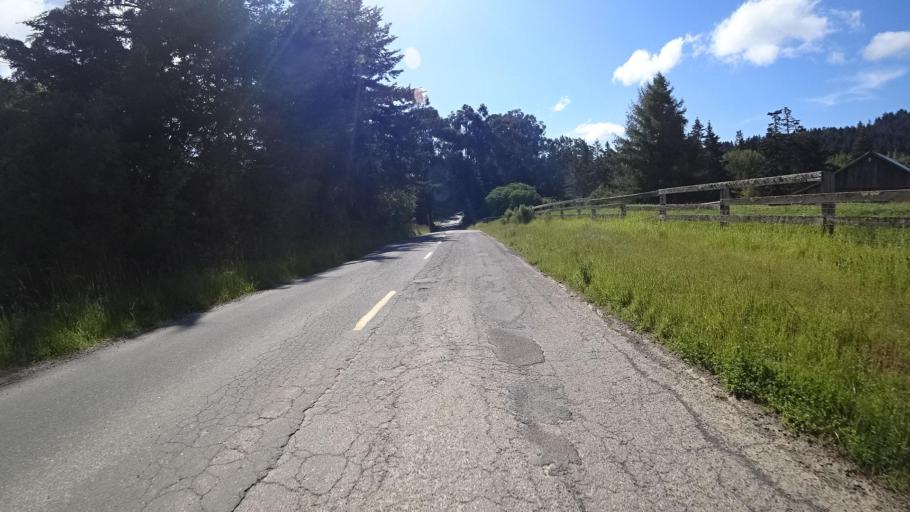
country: US
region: California
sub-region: Humboldt County
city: Ferndale
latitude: 40.3475
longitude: -124.3300
